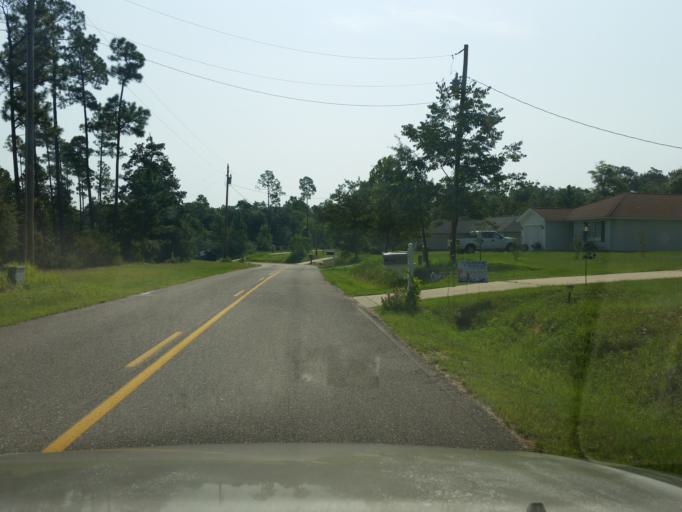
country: US
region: Florida
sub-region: Escambia County
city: Bellview
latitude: 30.5104
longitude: -87.4583
